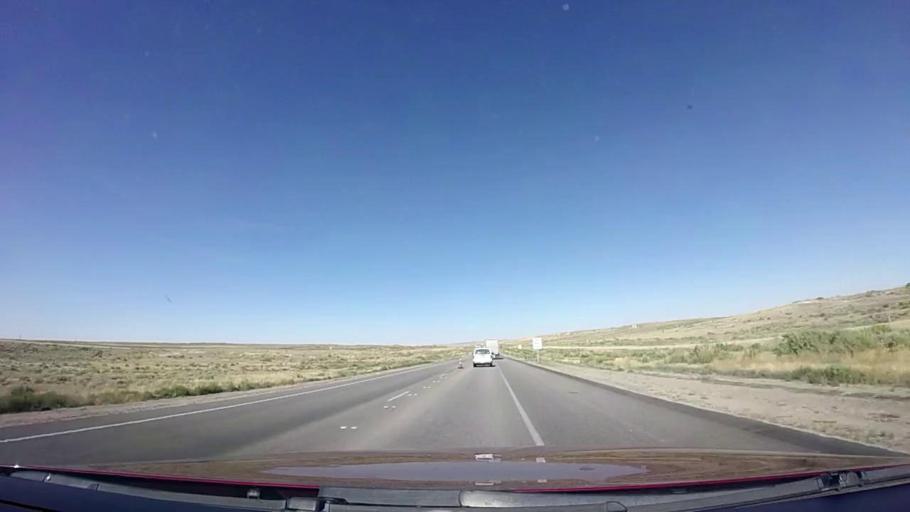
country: US
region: Wyoming
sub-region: Carbon County
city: Rawlins
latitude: 41.7058
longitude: -107.8514
